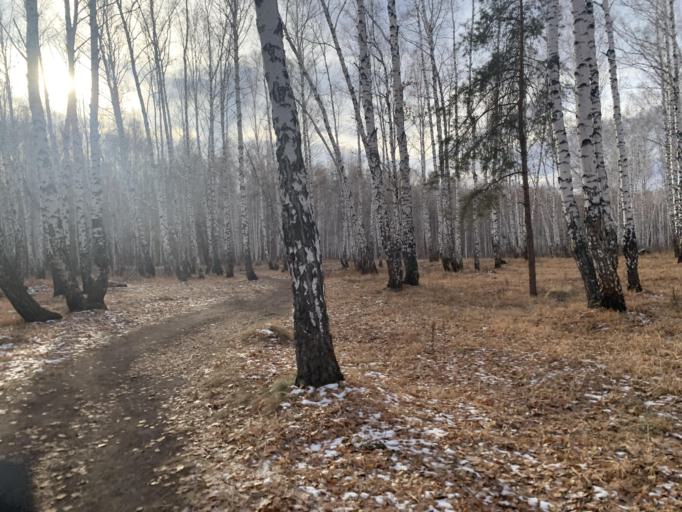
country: RU
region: Chelyabinsk
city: Roshchino
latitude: 55.2027
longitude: 61.3037
